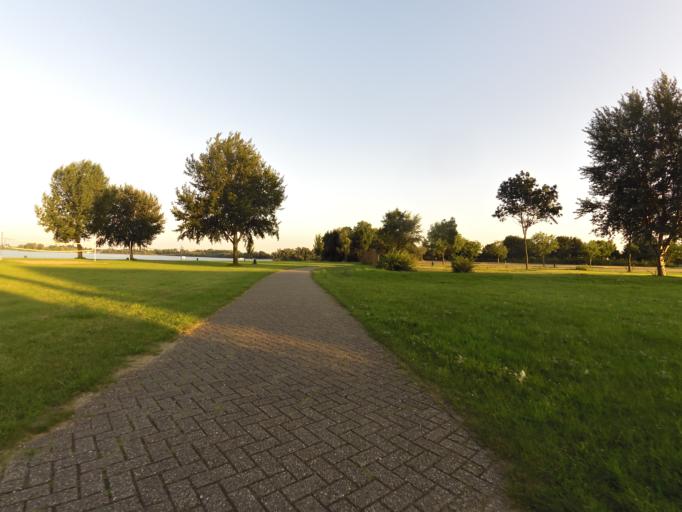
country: NL
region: Gelderland
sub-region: Gemeente Zevenaar
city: Zevenaar
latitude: 51.8674
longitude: 6.0780
